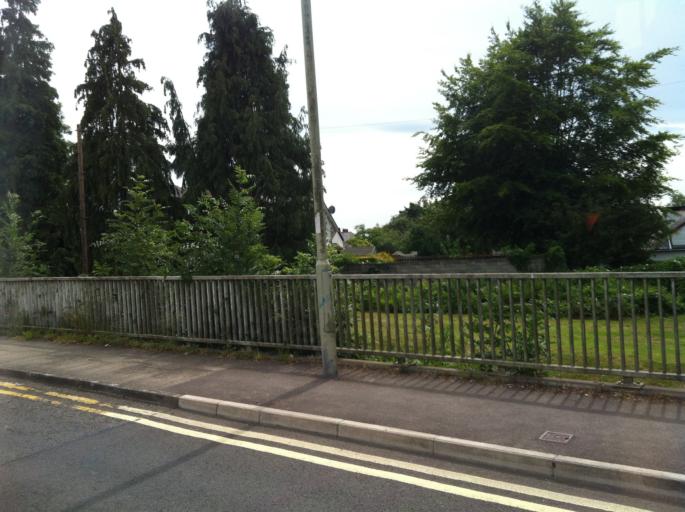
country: GB
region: Wales
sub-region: Bridgend county borough
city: Bridgend
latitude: 51.5032
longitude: -3.5799
